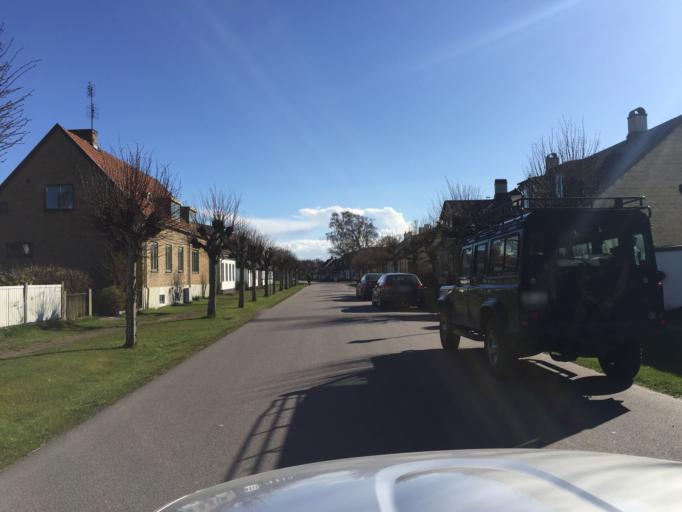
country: SE
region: Skane
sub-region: Vellinge Kommun
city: Skanor med Falsterbo
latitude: 55.4160
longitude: 12.8473
